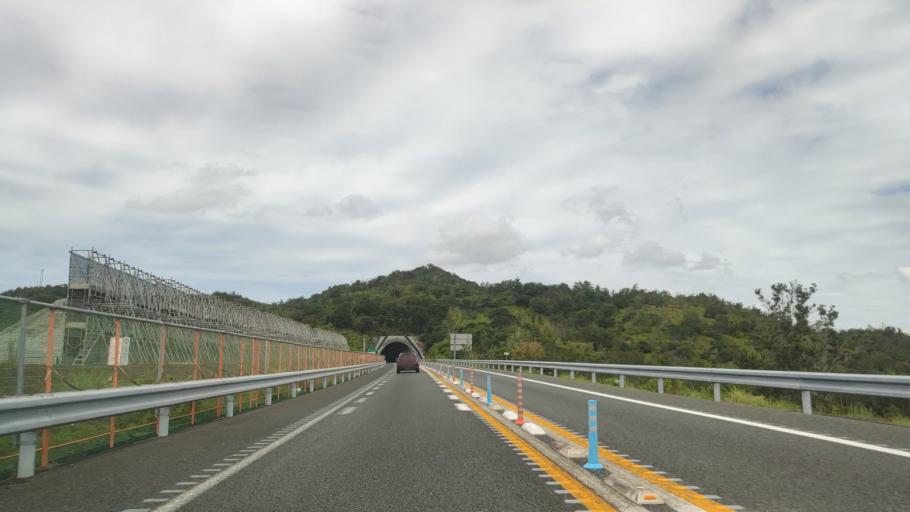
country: JP
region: Wakayama
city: Gobo
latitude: 33.8742
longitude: 135.1878
